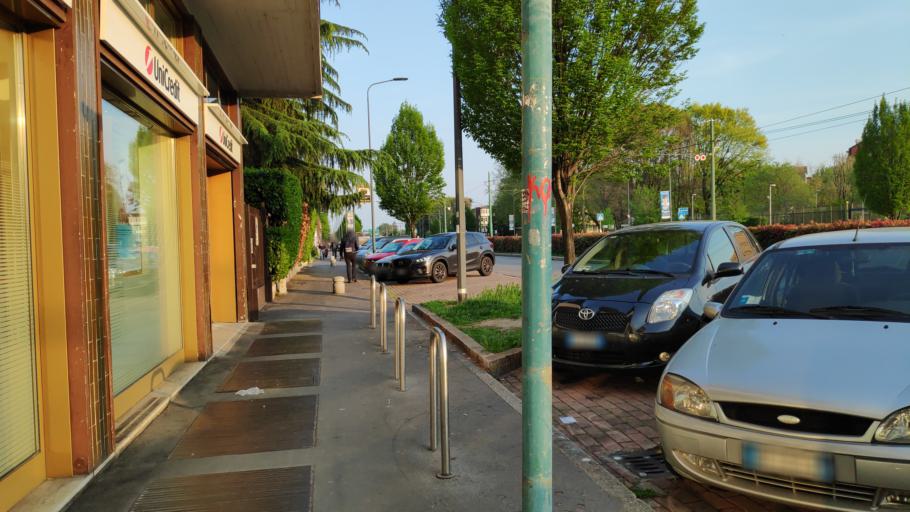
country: IT
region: Lombardy
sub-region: Citta metropolitana di Milano
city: Linate
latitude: 45.4500
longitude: 9.2523
